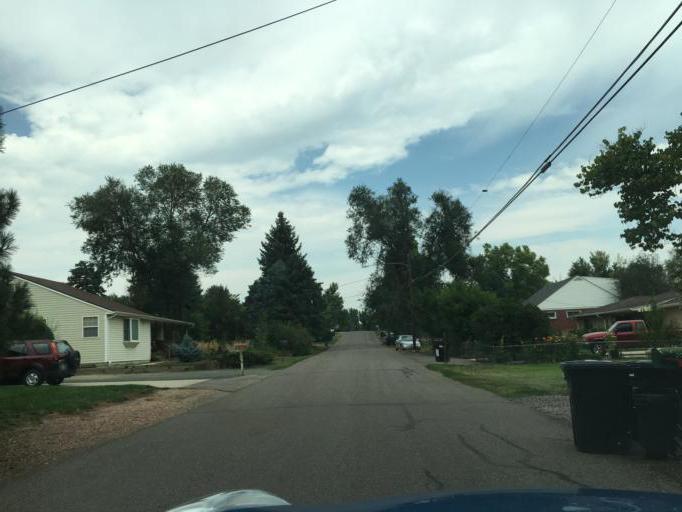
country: US
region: Colorado
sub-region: Jefferson County
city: Wheat Ridge
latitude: 39.7477
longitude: -105.0983
